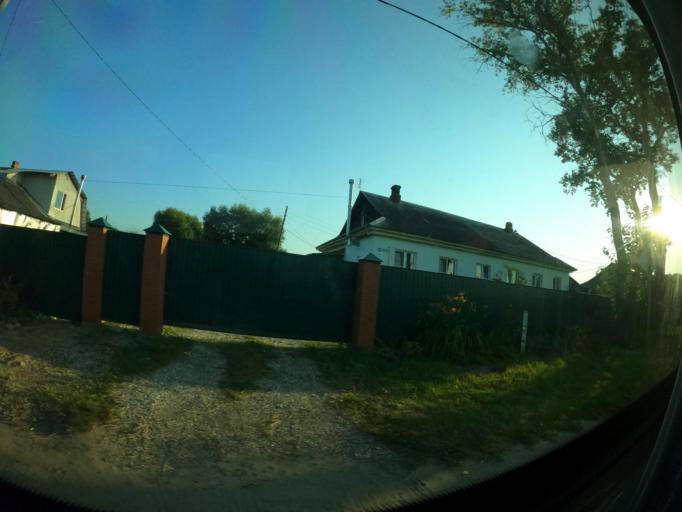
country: RU
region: Moskovskaya
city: Serpukhov
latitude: 54.9387
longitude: 37.3580
